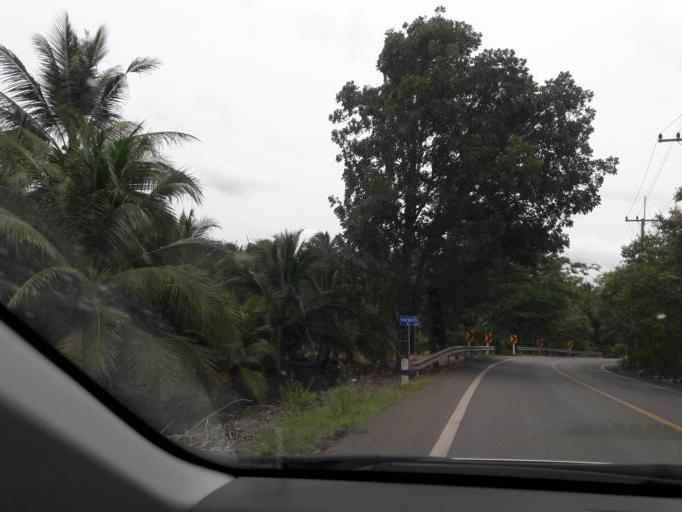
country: TH
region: Samut Sakhon
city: Ban Phaeo
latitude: 13.6172
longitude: 100.0230
